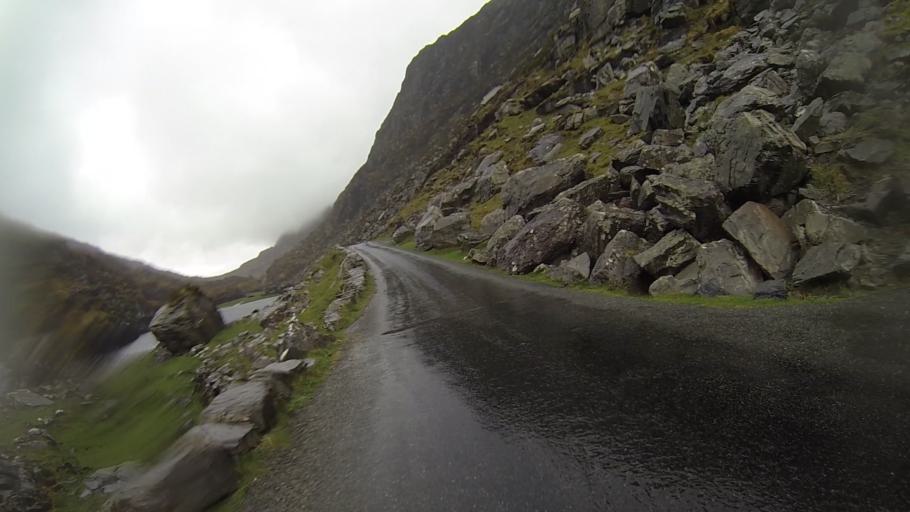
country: IE
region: Munster
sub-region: Ciarrai
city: Cill Airne
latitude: 52.0068
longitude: -9.6423
